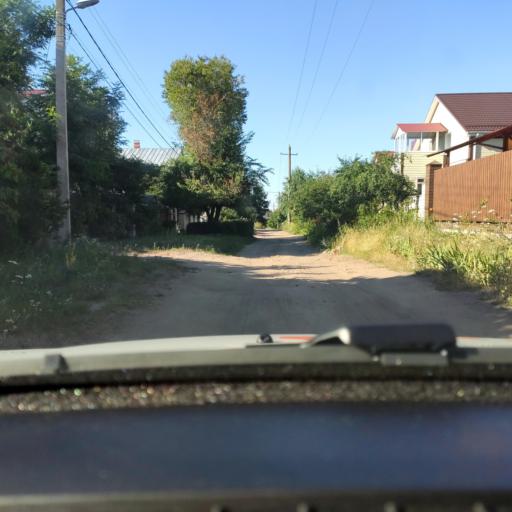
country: RU
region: Voronezj
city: Pridonskoy
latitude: 51.6278
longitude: 39.0889
